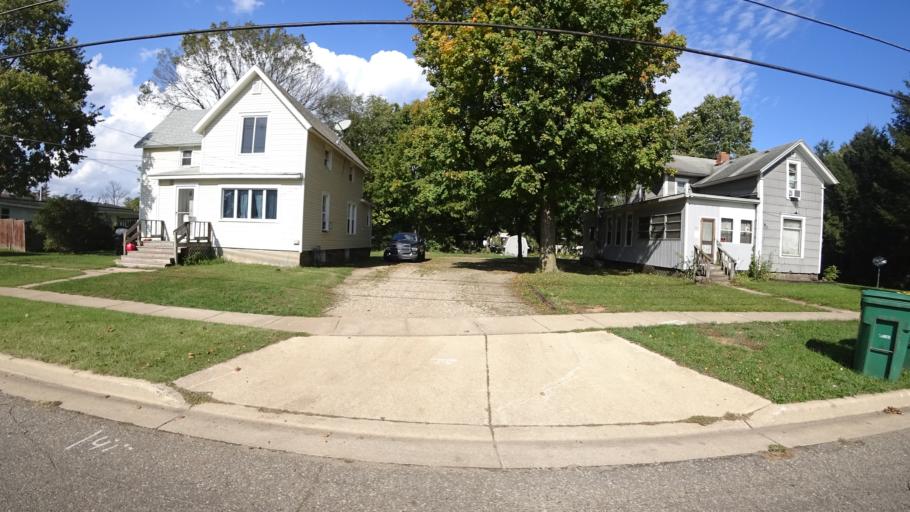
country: US
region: Michigan
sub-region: Saint Joseph County
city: Three Rivers
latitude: 41.9391
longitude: -85.6278
